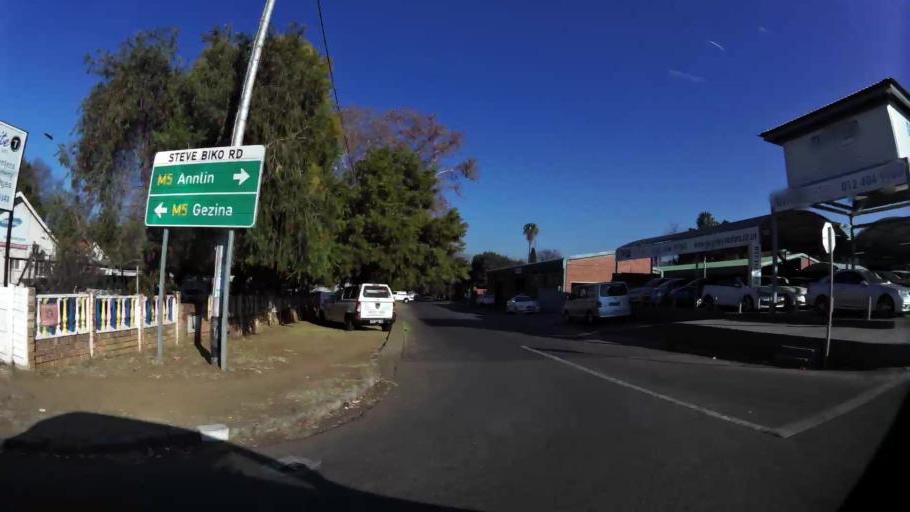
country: ZA
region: Gauteng
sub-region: City of Tshwane Metropolitan Municipality
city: Pretoria
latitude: -25.7031
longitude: 28.1999
